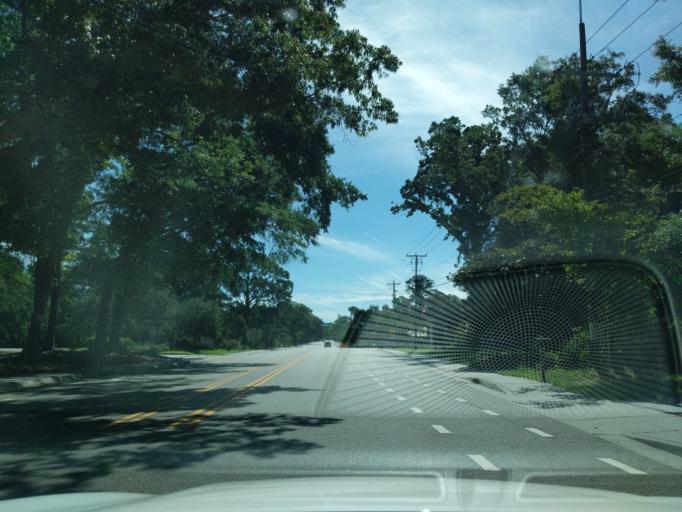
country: US
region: South Carolina
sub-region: Charleston County
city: Charleston
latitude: 32.7422
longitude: -79.9310
